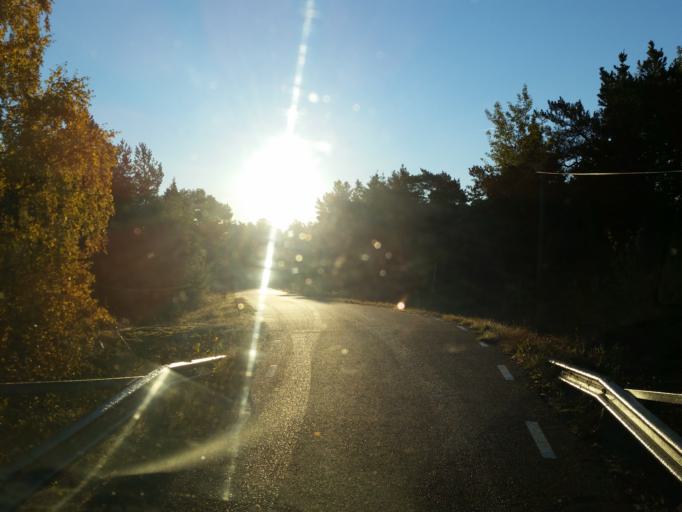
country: AX
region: Alands skaergard
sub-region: Vardoe
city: Vardoe
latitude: 60.3476
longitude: 20.3317
